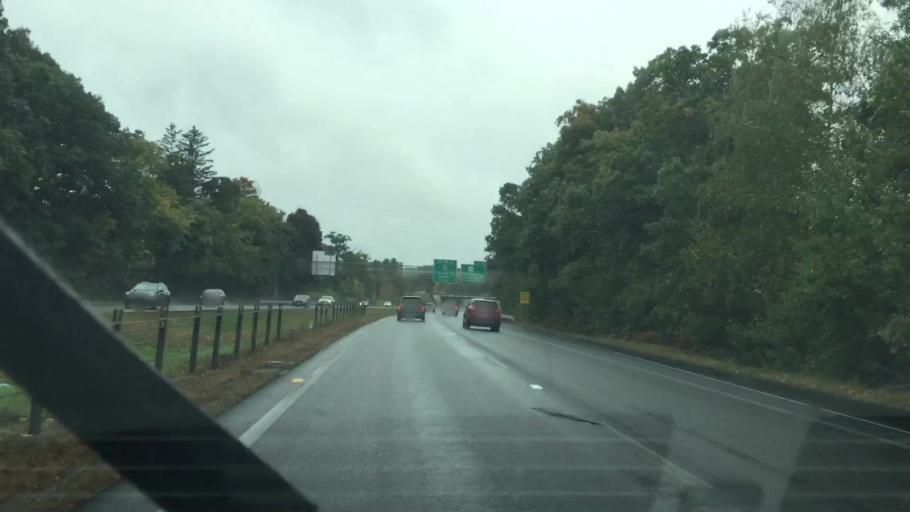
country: US
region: Massachusetts
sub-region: Essex County
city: Methuen
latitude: 42.7347
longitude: -71.1857
